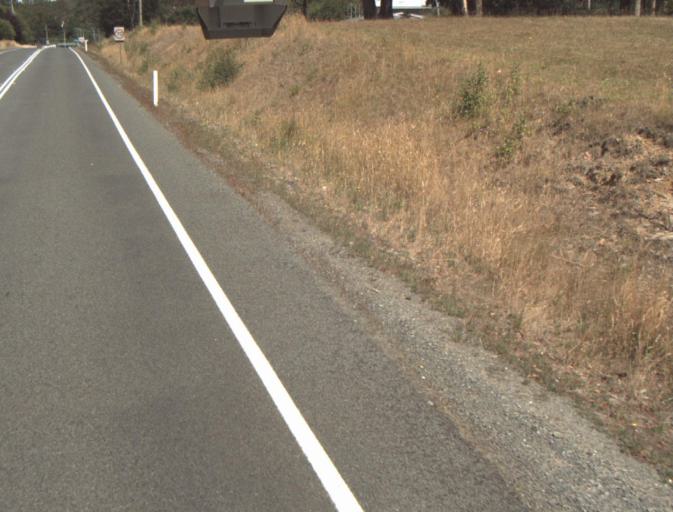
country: AU
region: Tasmania
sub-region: Launceston
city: Newstead
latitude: -41.3864
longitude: 147.3069
